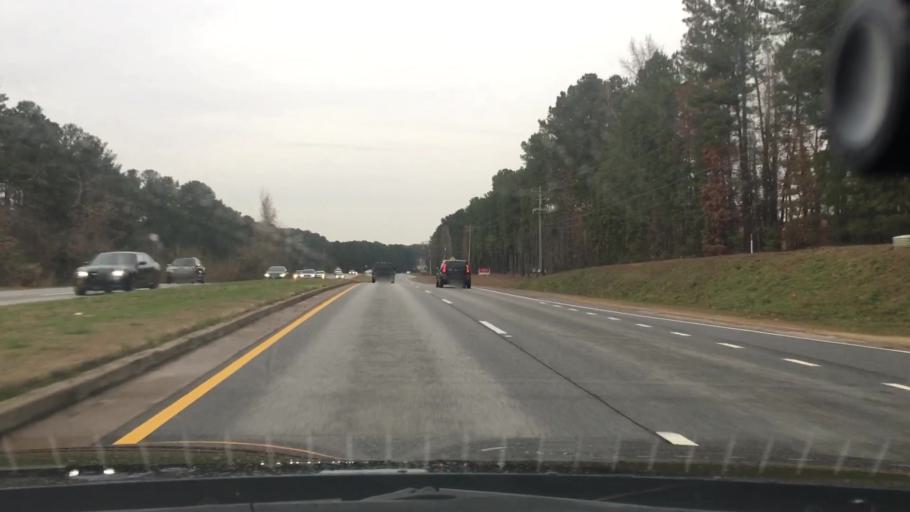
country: US
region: Georgia
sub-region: Fayette County
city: Peachtree City
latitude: 33.4170
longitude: -84.6031
